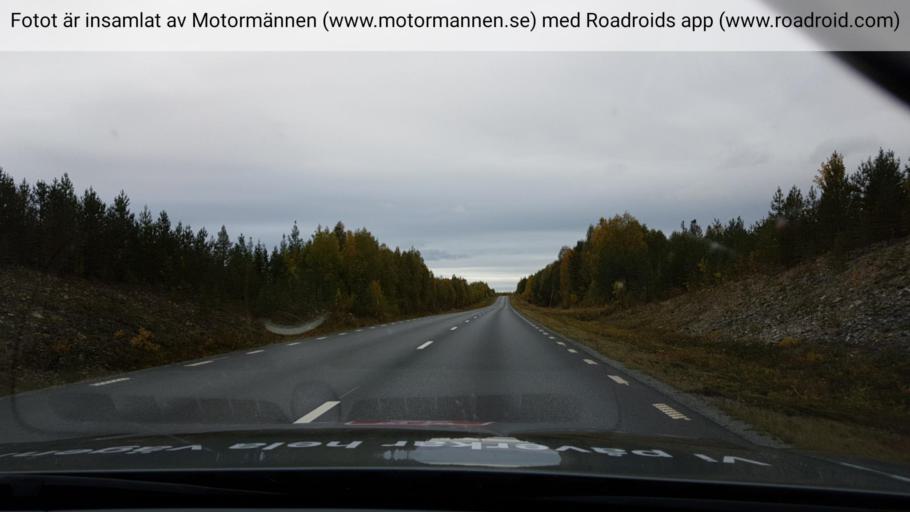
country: SE
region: Vaesterbotten
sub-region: Dorotea Kommun
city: Dorotea
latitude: 64.3280
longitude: 16.6267
